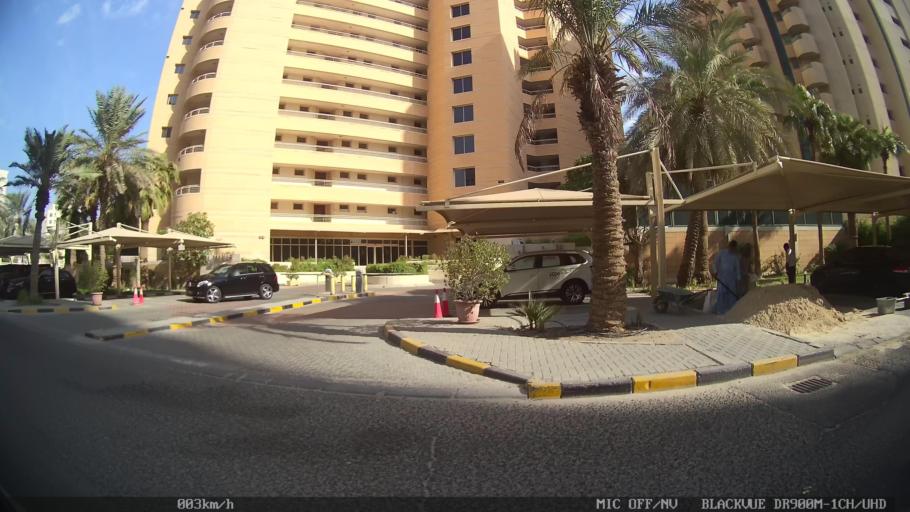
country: KW
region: Al Asimah
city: Ad Dasmah
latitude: 29.3685
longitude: 48.0106
